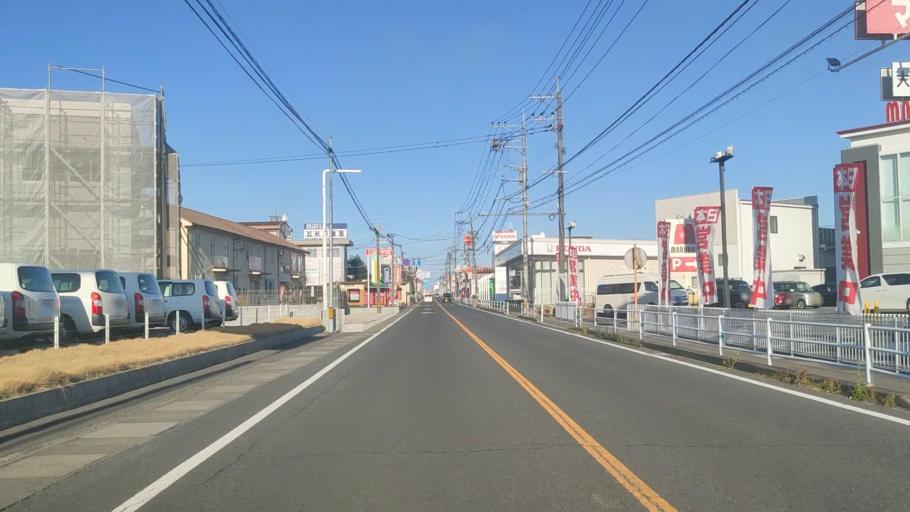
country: JP
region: Oita
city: Oita
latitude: 33.2132
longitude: 131.6095
